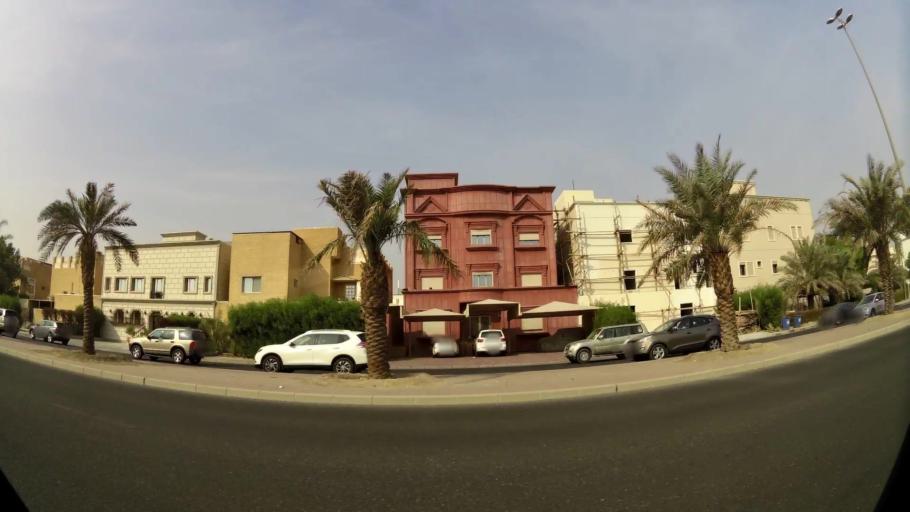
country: KW
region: Al Asimah
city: Ar Rabiyah
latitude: 29.2801
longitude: 47.9317
